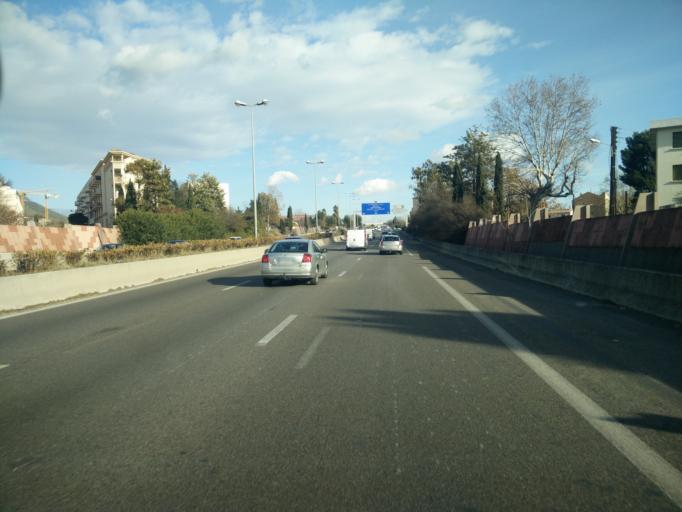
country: FR
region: Provence-Alpes-Cote d'Azur
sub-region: Departement du Var
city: La Valette-du-Var
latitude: 43.1243
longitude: 5.9654
